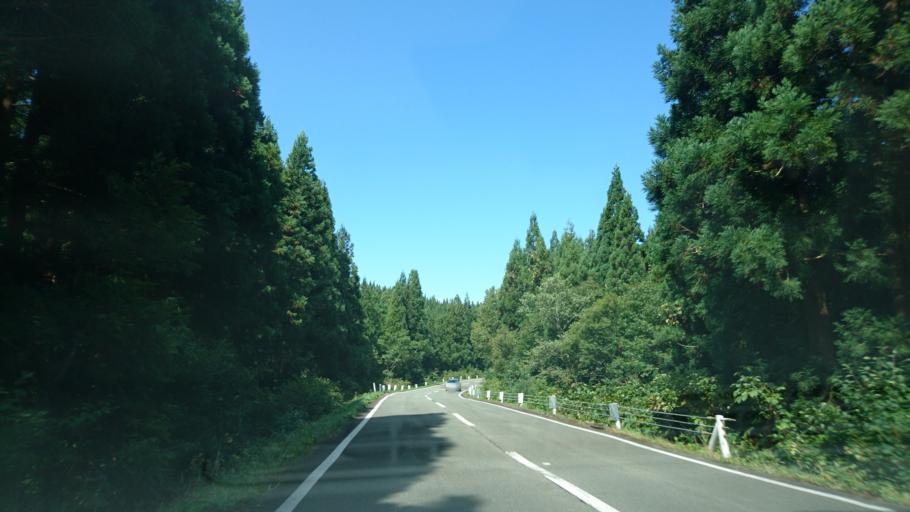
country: JP
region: Akita
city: Yuzawa
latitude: 38.9726
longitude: 140.7106
